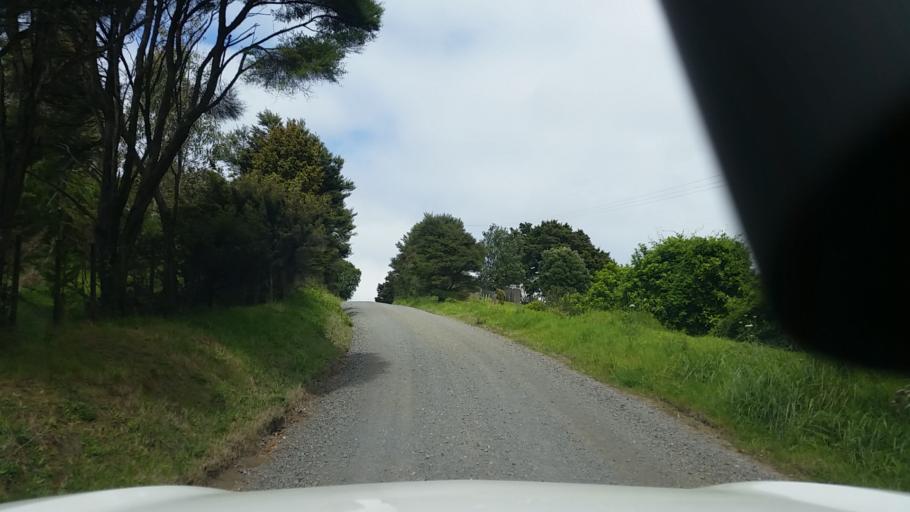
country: NZ
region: Auckland
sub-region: Auckland
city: Muriwai Beach
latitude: -36.8432
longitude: 174.5121
